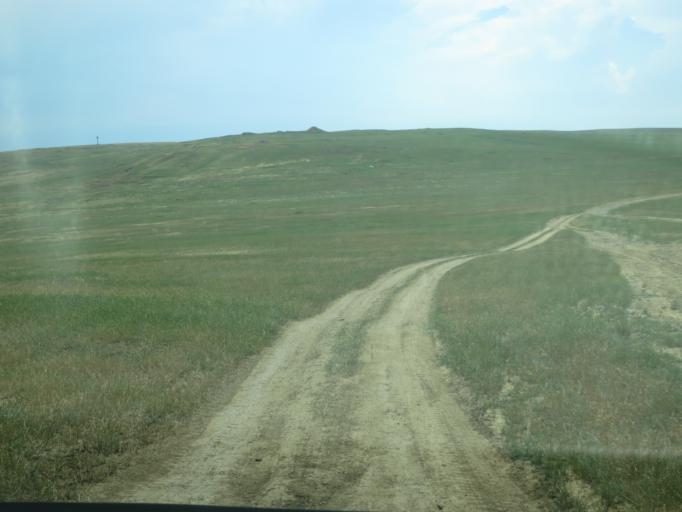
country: AZ
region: Agstafa
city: Saloglu
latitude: 41.4749
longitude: 45.3023
